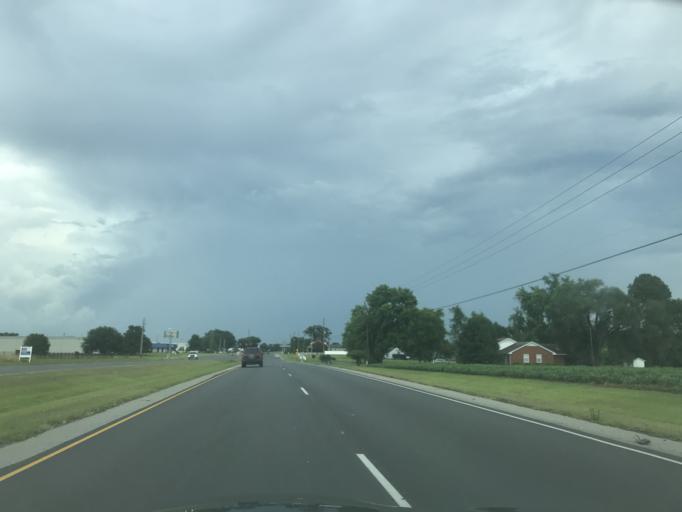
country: US
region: North Carolina
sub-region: Johnston County
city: Clayton
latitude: 35.6263
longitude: -78.4280
